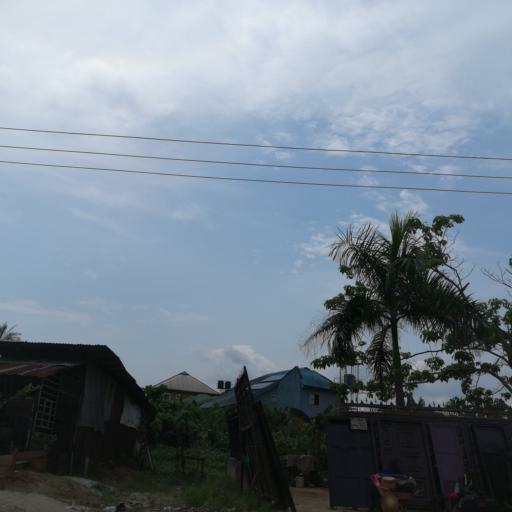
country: NG
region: Rivers
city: Port Harcourt
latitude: 4.8623
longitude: 7.0206
